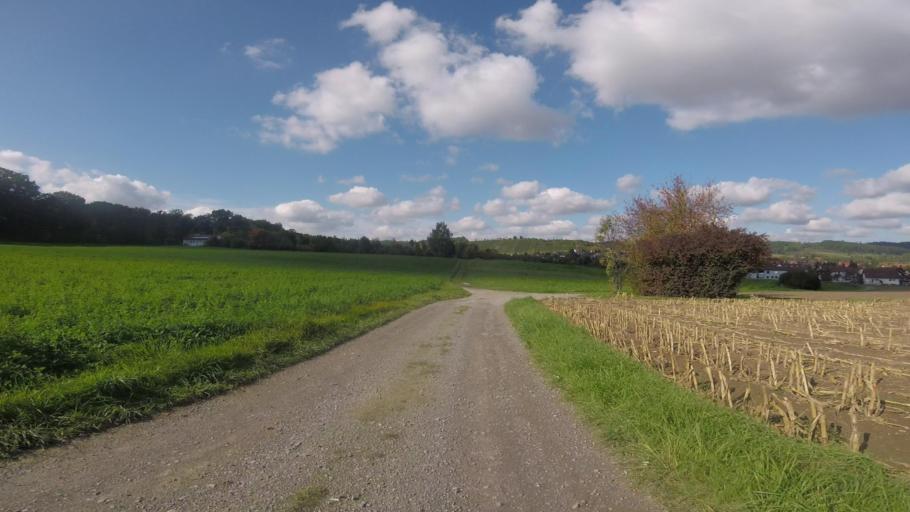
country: DE
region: Baden-Wuerttemberg
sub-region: Regierungsbezirk Stuttgart
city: Aspach
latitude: 48.9867
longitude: 9.3586
